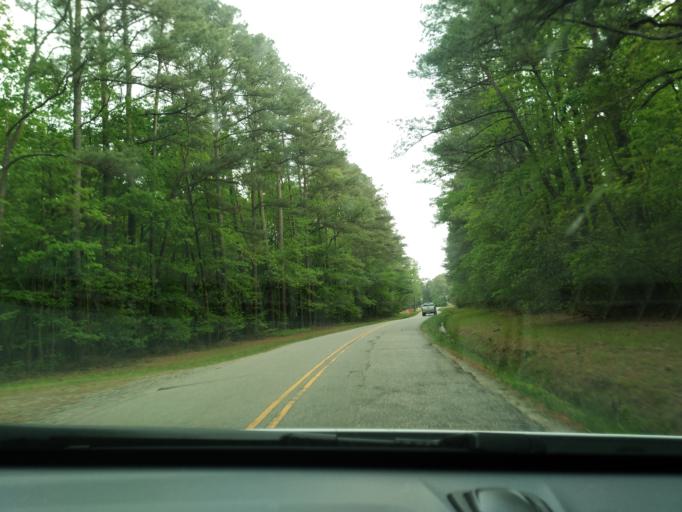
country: US
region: Virginia
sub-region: York County
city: Yorktown
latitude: 37.1754
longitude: -76.5147
